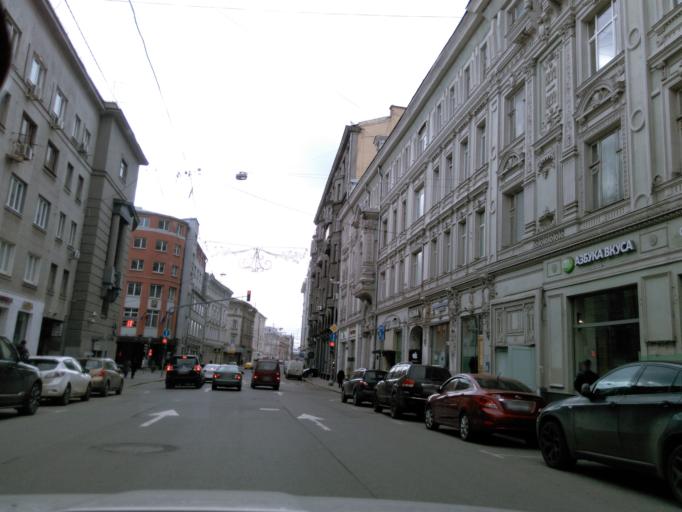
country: RU
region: Moscow
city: Moscow
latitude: 55.7653
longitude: 37.6161
